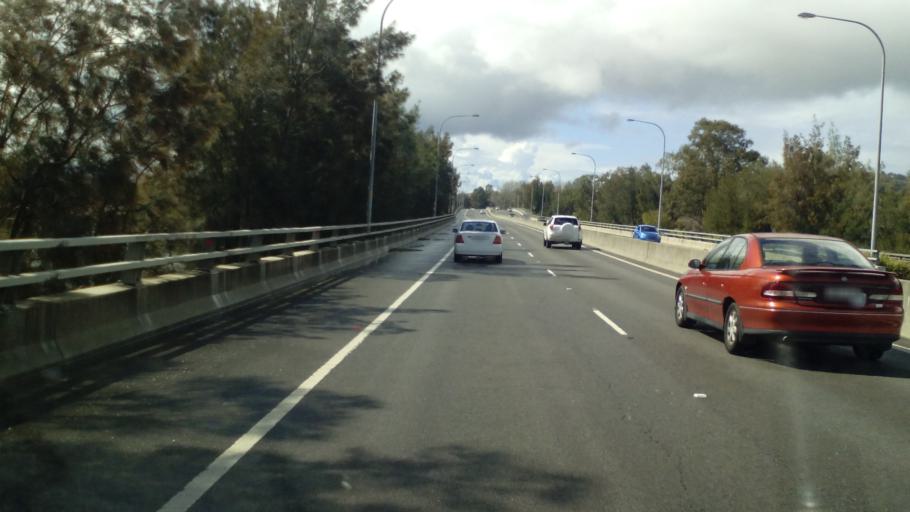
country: AU
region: New South Wales
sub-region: Lake Macquarie Shire
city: Fennell Bay
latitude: -32.9613
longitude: 151.6113
